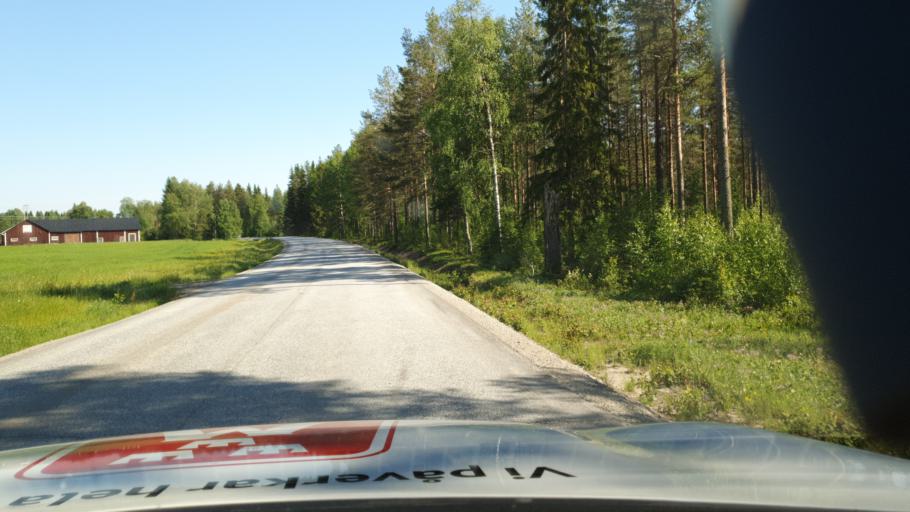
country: SE
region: Vaesterbotten
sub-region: Vindelns Kommun
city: Vindeln
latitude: 64.1790
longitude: 19.7218
